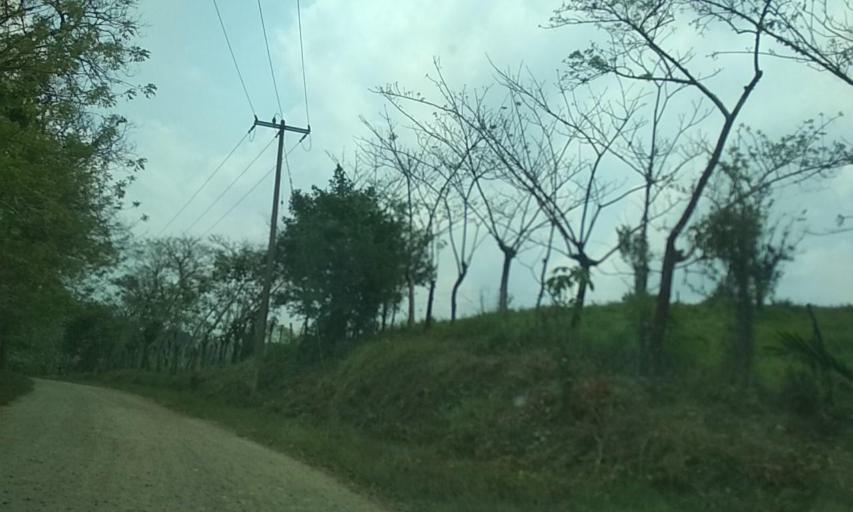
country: MX
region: Tabasco
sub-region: Huimanguillo
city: Francisco Rueda
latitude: 17.6015
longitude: -93.8015
